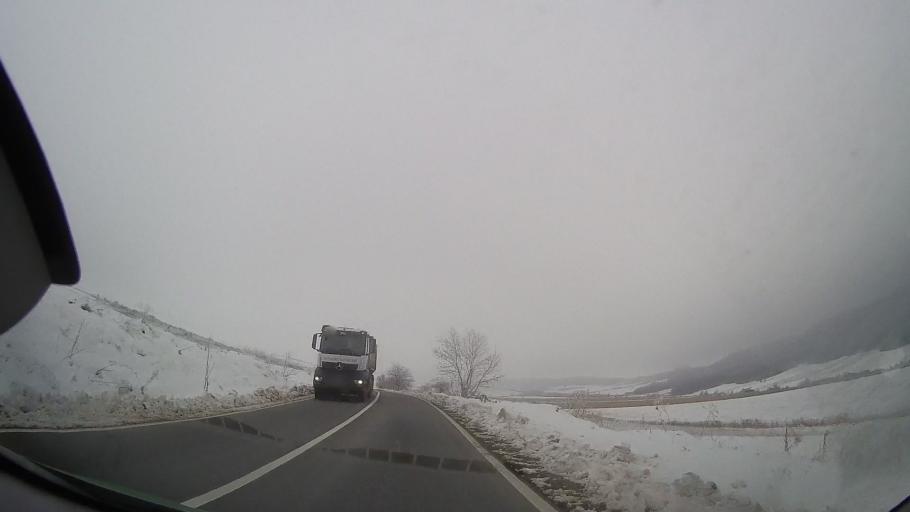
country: RO
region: Neamt
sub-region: Comuna Poenari
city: Poienari
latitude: 46.8720
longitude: 27.1423
